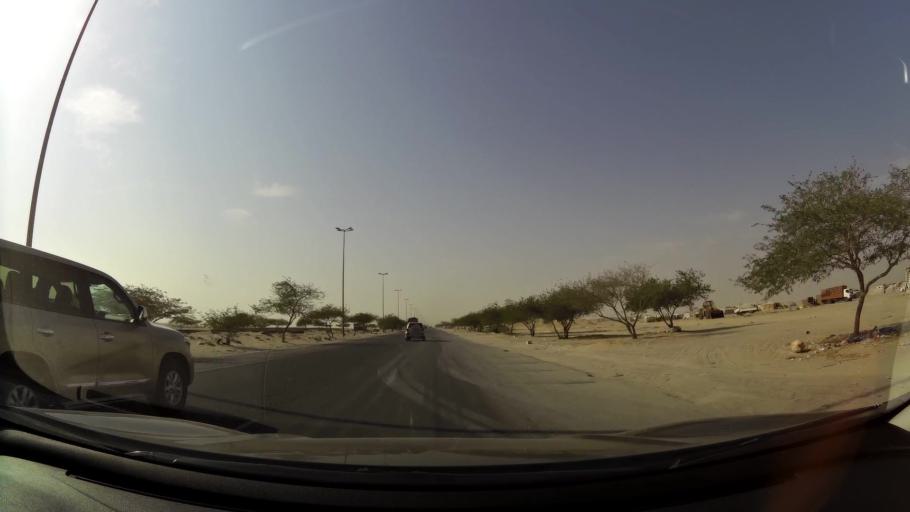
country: KW
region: Al Ahmadi
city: Al Ahmadi
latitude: 28.9327
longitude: 48.1080
